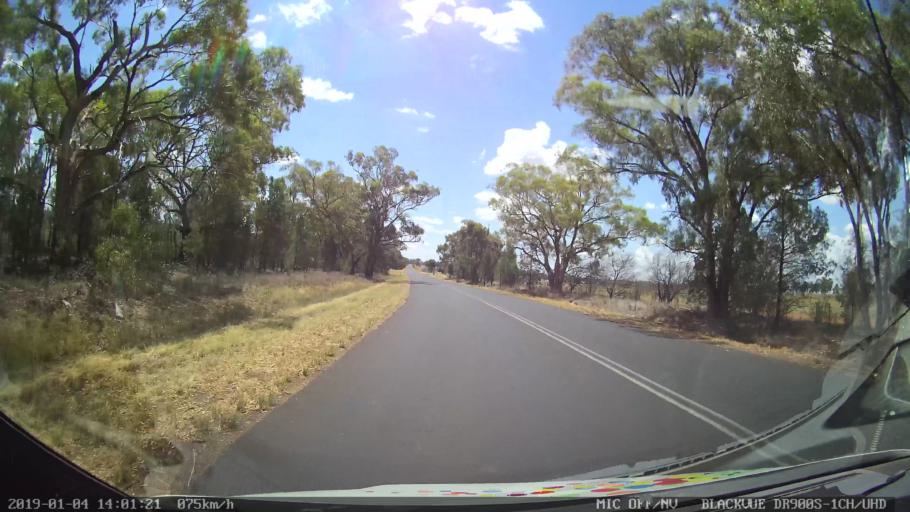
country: AU
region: New South Wales
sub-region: Dubbo Municipality
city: Dubbo
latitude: -32.2978
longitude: 148.5994
